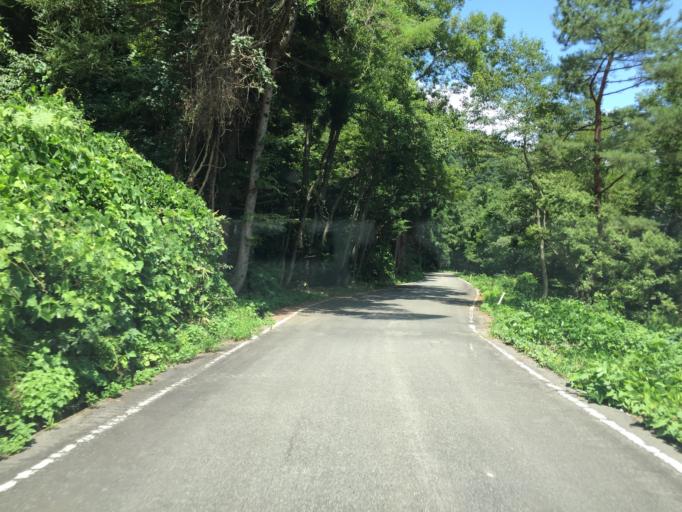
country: JP
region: Fukushima
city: Inawashiro
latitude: 37.4869
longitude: 140.0294
